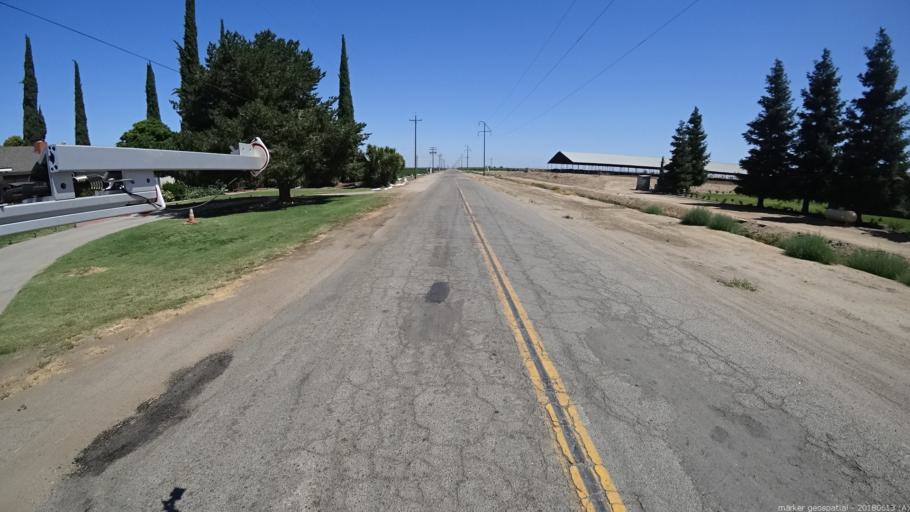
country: US
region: California
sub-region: Madera County
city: Chowchilla
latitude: 37.0617
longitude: -120.3469
